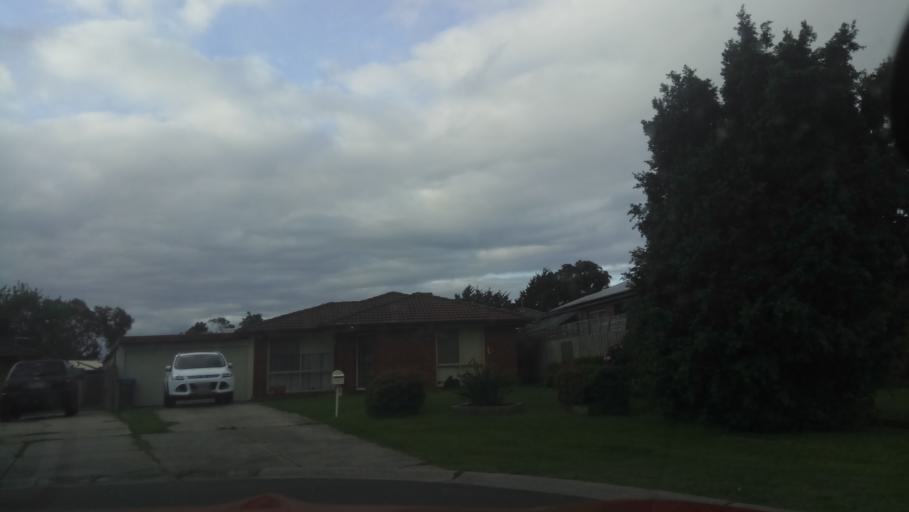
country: AU
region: Victoria
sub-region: Casey
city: Cranbourne North
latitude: -38.0738
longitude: 145.2668
